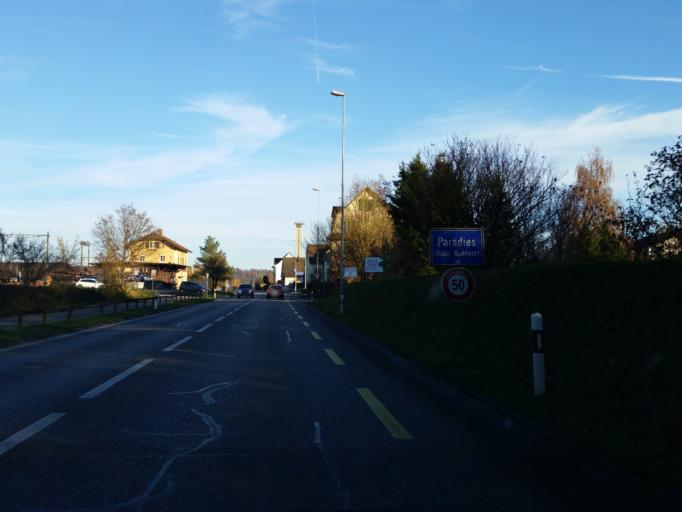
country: DE
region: Baden-Wuerttemberg
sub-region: Freiburg Region
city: Busingen
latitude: 47.6792
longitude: 8.6856
